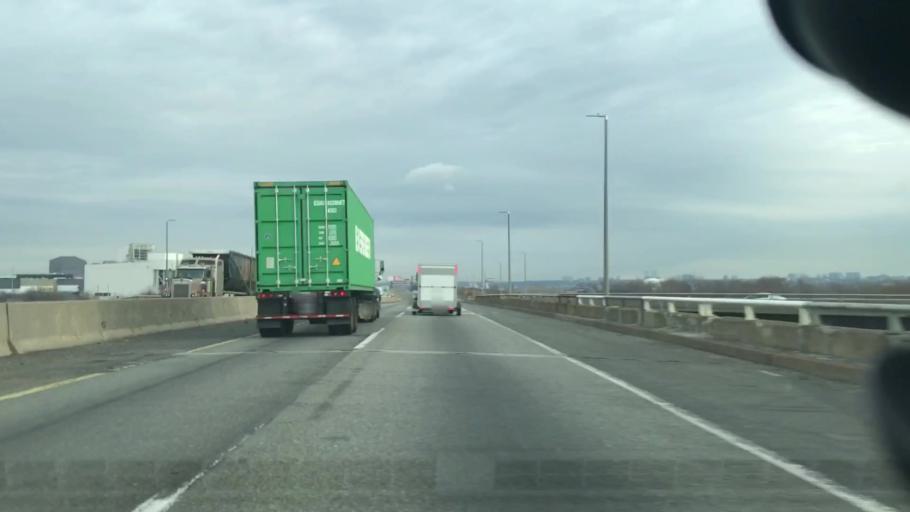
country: US
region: New Jersey
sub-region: Hudson County
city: Secaucus
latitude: 40.7999
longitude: -74.0756
